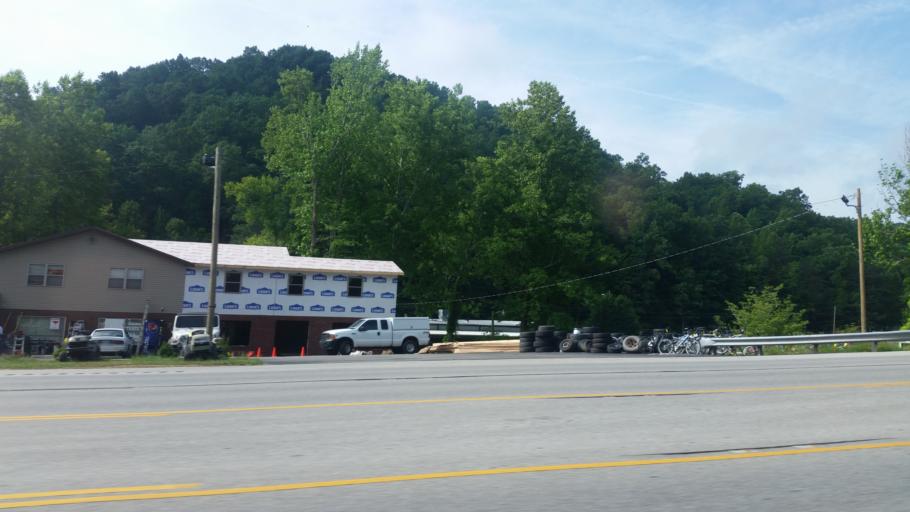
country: US
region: Kentucky
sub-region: Rowan County
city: Morehead
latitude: 38.1797
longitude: -83.4537
